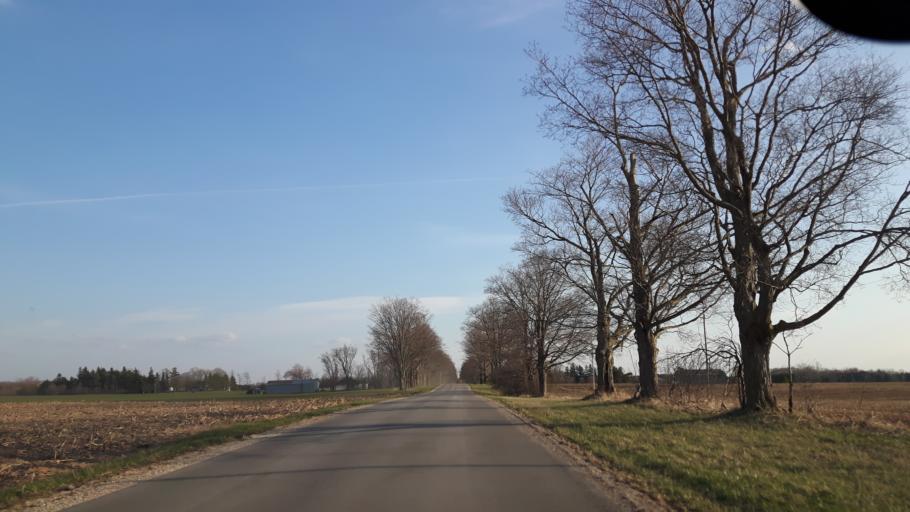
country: CA
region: Ontario
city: Goderich
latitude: 43.6294
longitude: -81.6646
